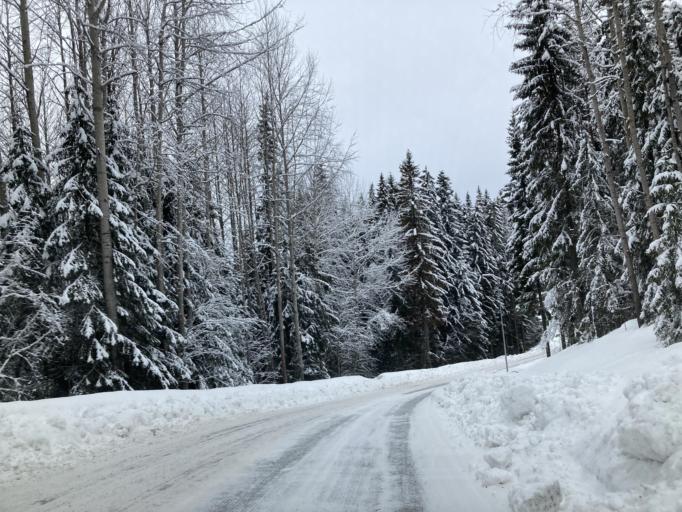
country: FI
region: Central Finland
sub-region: Jaemsae
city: Jaemsae
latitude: 61.8784
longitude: 25.3071
